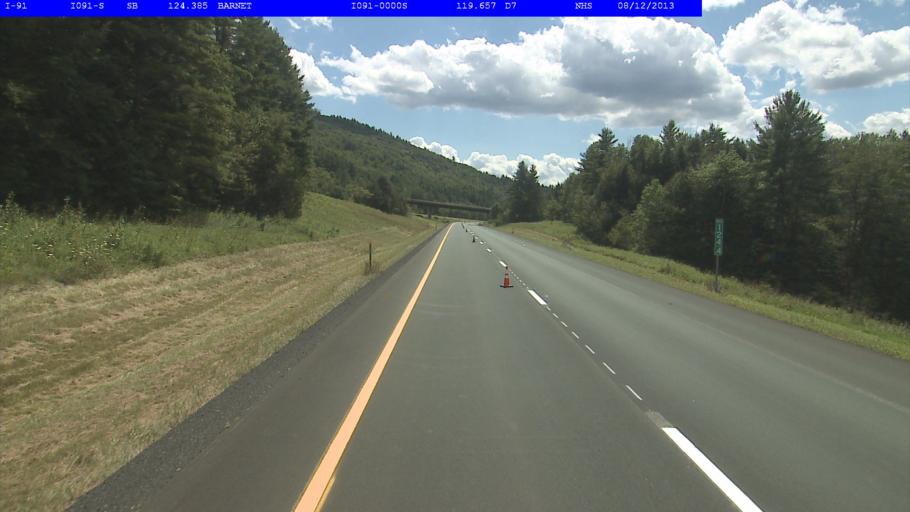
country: US
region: Vermont
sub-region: Caledonia County
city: Saint Johnsbury
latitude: 44.3437
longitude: -72.0334
